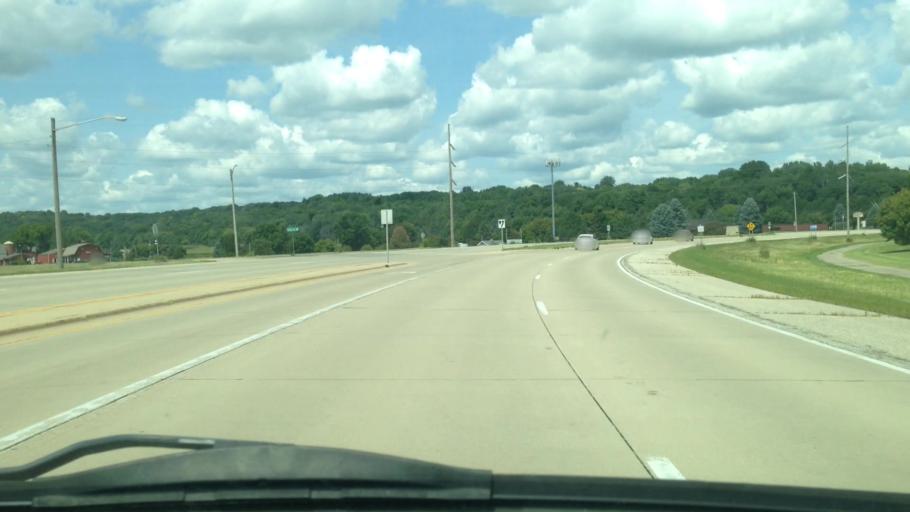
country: US
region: Minnesota
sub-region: Olmsted County
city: Rochester
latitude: 44.0037
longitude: -92.5069
